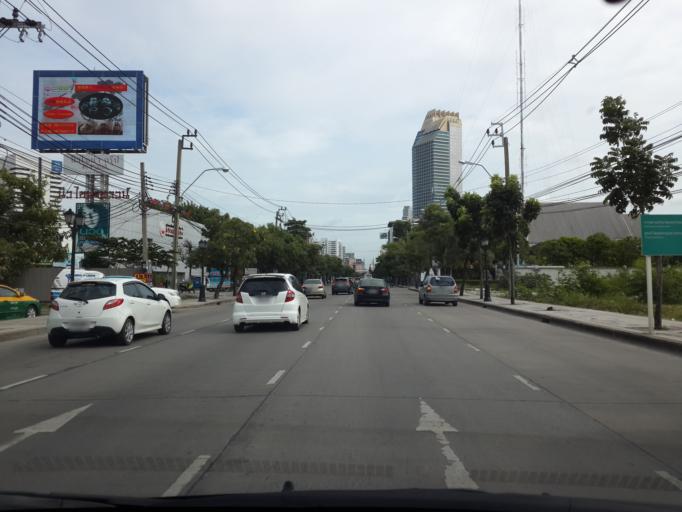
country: TH
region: Bangkok
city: Huai Khwang
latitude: 13.7638
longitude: 100.5726
